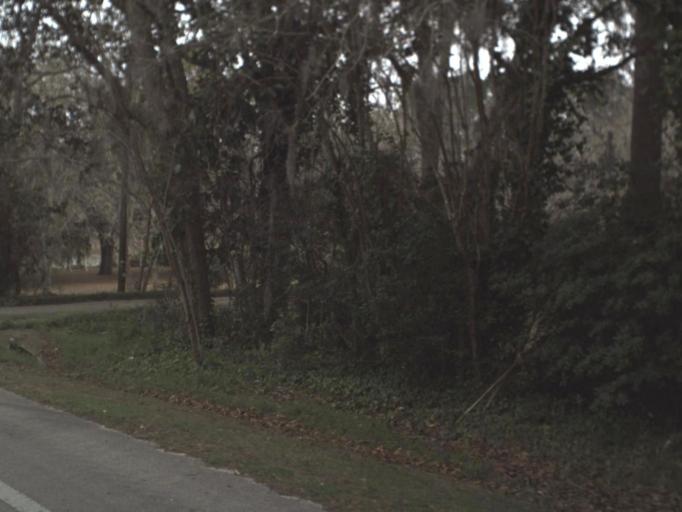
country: US
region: Florida
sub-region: Jefferson County
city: Monticello
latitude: 30.5450
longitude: -83.8893
